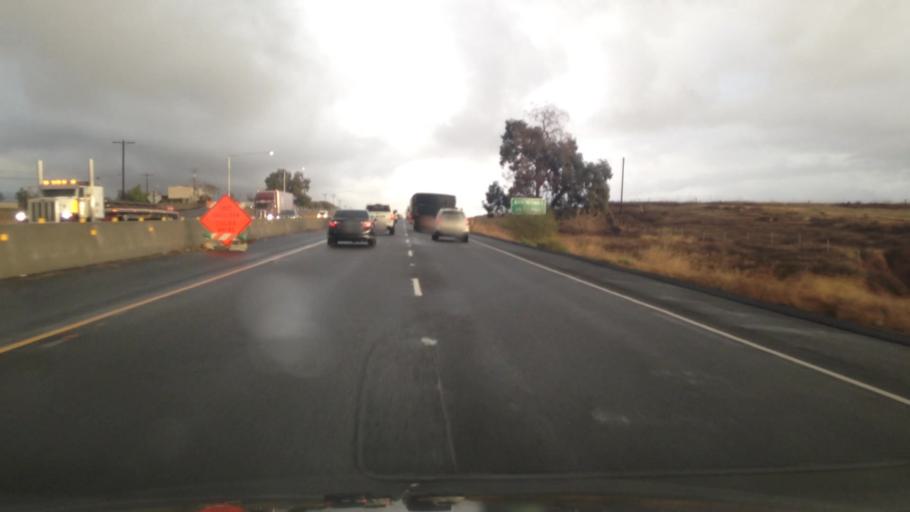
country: US
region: California
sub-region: Riverside County
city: Beaumont
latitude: 33.9335
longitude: -117.0102
